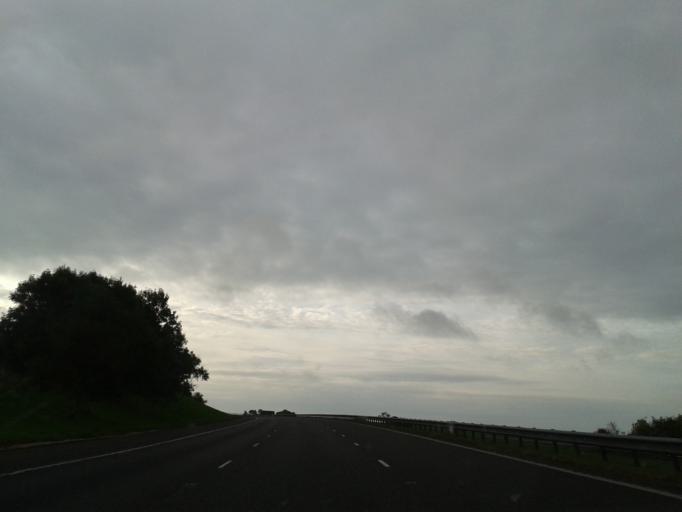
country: GB
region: Scotland
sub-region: Dumfries and Galloway
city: Lockerbie
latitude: 55.0825
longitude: -3.3160
